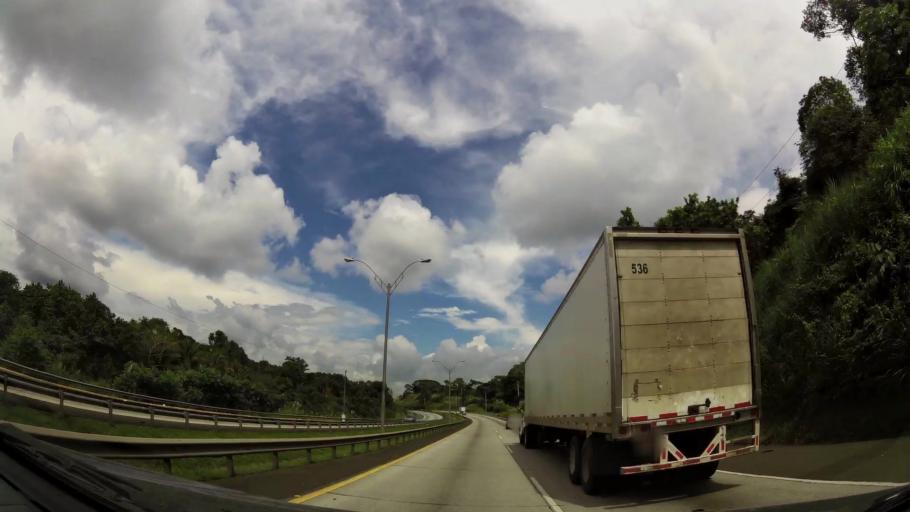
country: PA
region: Panama
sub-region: Distrito de Panama
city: Paraiso
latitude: 9.0014
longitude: -79.6507
